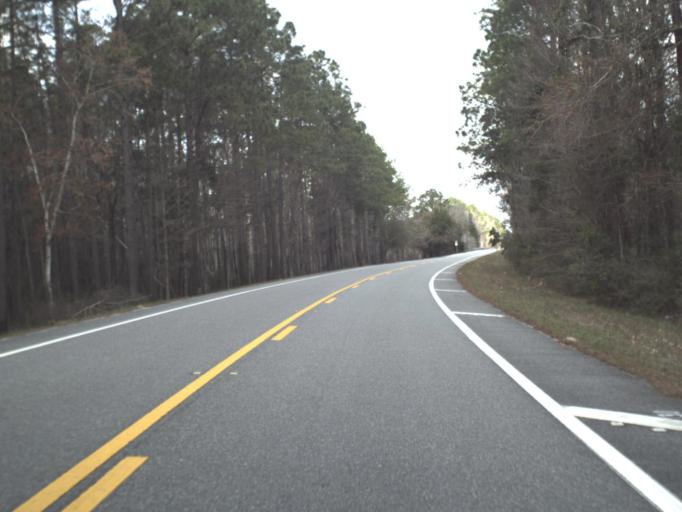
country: US
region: Florida
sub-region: Franklin County
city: Apalachicola
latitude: 29.8506
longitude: -84.9726
